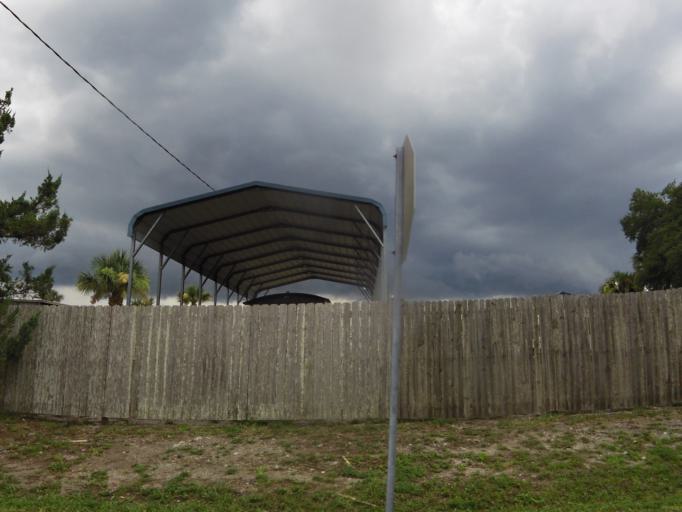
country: US
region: Florida
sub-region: Duval County
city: Atlantic Beach
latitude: 30.3255
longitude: -81.4218
